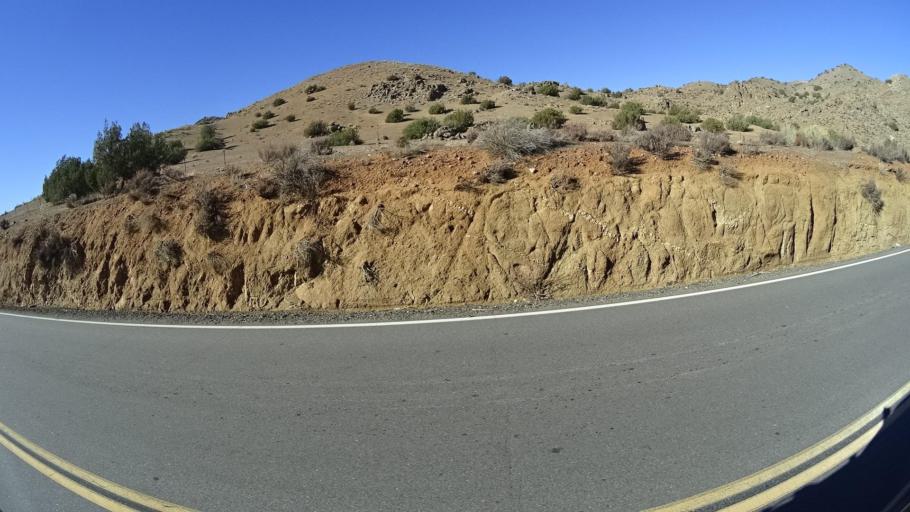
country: US
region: California
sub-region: Kern County
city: Wofford Heights
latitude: 35.6829
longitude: -118.3862
